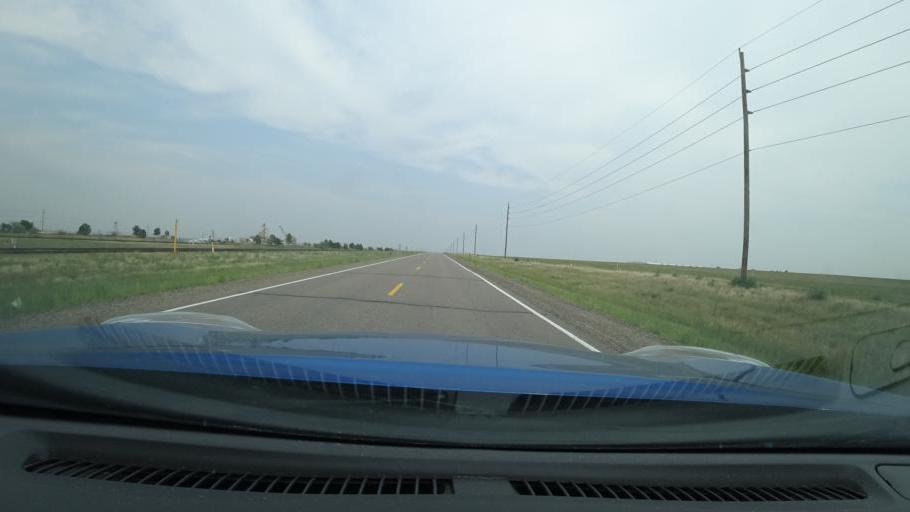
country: US
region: Colorado
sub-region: Adams County
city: Aurora
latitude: 39.7513
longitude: -104.7450
